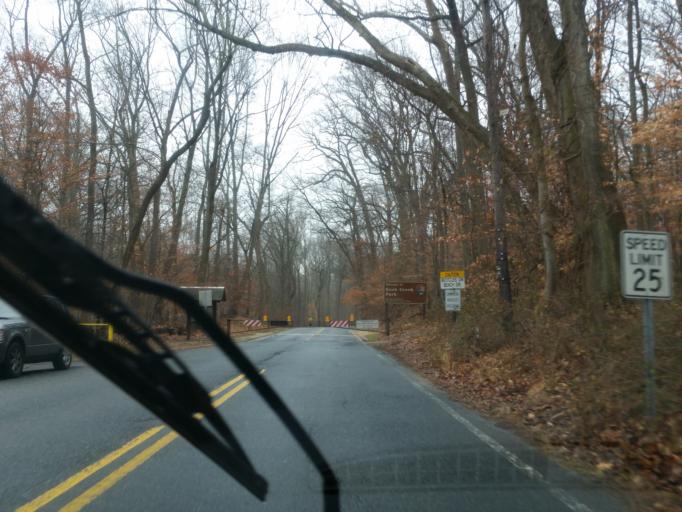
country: US
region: Maryland
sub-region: Montgomery County
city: Chevy Chase
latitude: 38.9864
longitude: -77.0535
